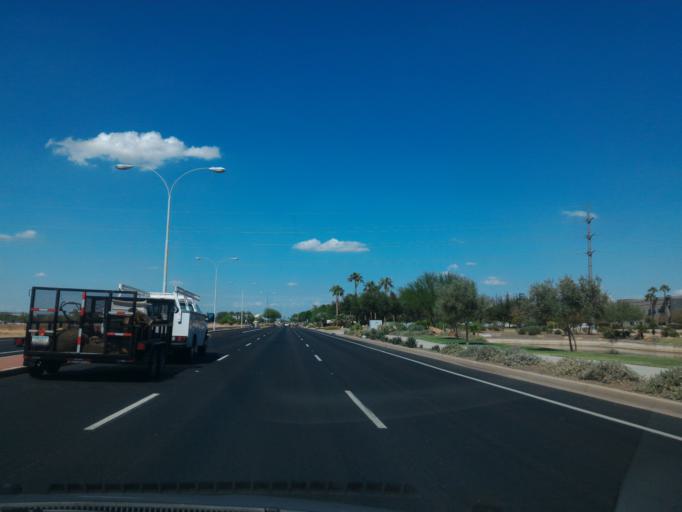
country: US
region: Arizona
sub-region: Maricopa County
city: Chandler
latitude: 33.2715
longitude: -111.8891
